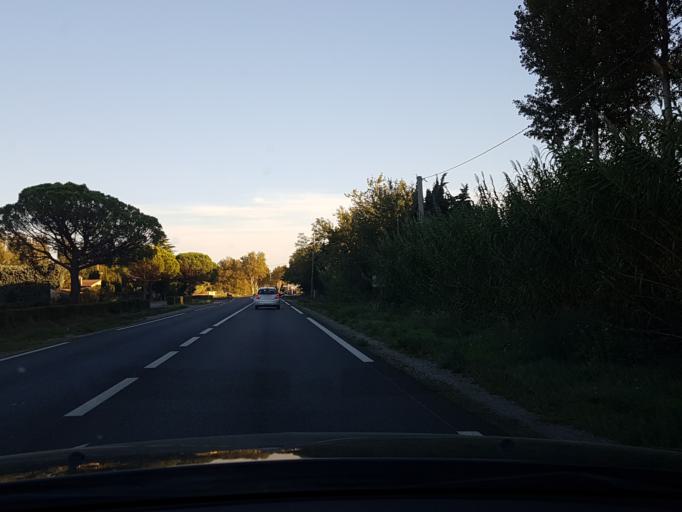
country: FR
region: Provence-Alpes-Cote d'Azur
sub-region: Departement des Bouches-du-Rhone
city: Saint-Andiol
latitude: 43.8474
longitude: 4.9299
